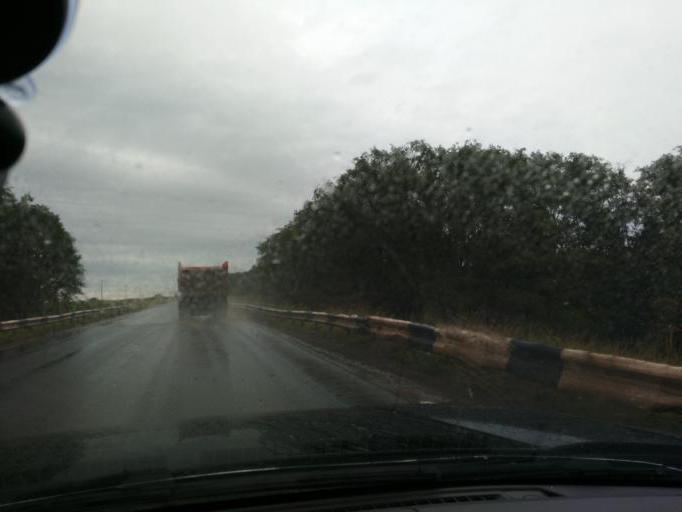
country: RU
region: Perm
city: Kultayevo
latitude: 57.8541
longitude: 55.8539
